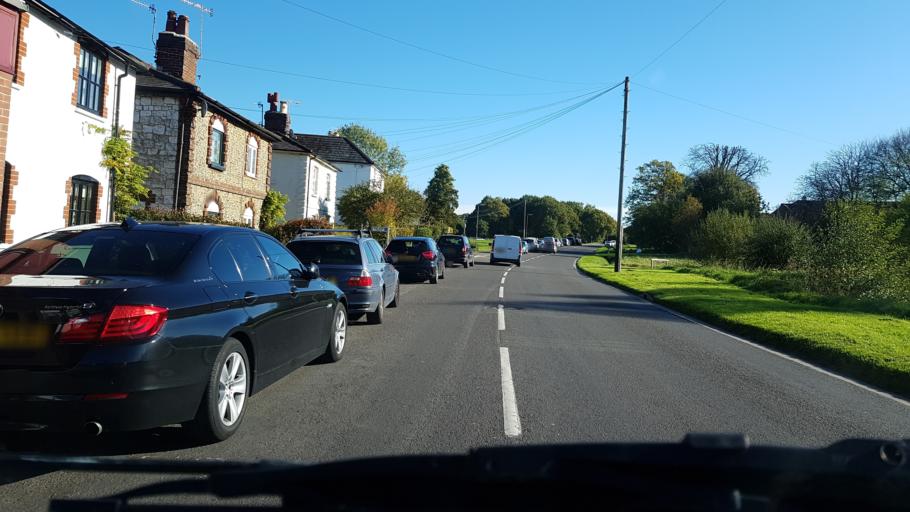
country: GB
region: England
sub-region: Surrey
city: Shalford
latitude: 51.2129
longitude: -0.5642
